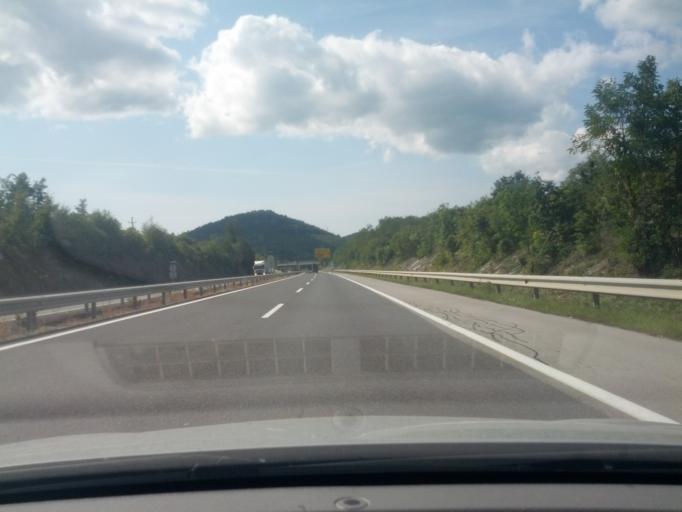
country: SI
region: Sezana
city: Sezana
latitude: 45.7136
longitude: 13.8907
